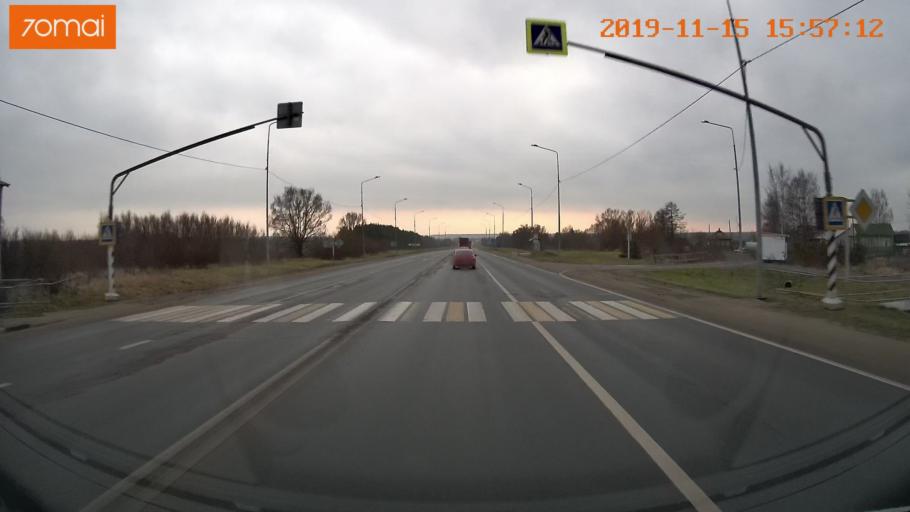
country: RU
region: Jaroslavl
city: Yaroslavl
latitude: 57.8330
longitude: 39.9659
